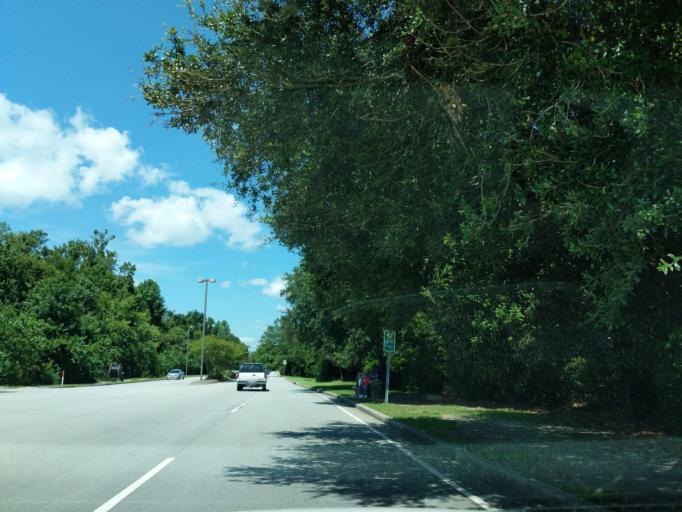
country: US
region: South Carolina
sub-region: Charleston County
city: North Charleston
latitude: 32.8677
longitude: -80.0160
